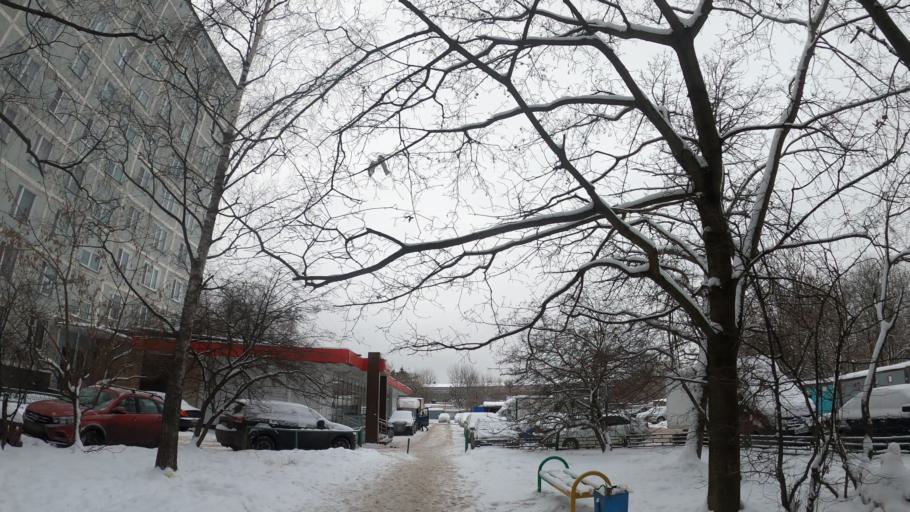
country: RU
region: Moskovskaya
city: Dolgoprudnyy
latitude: 55.9532
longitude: 37.4887
